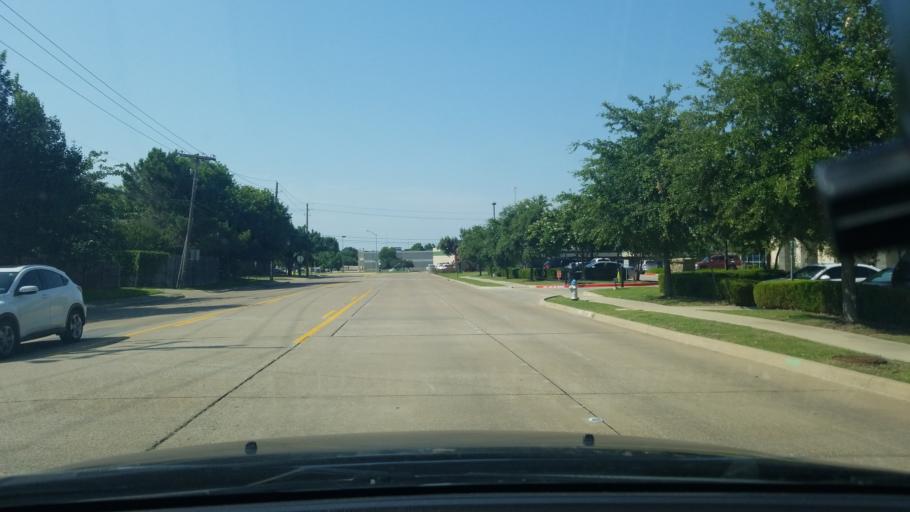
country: US
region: Texas
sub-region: Dallas County
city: Mesquite
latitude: 32.8171
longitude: -96.6270
